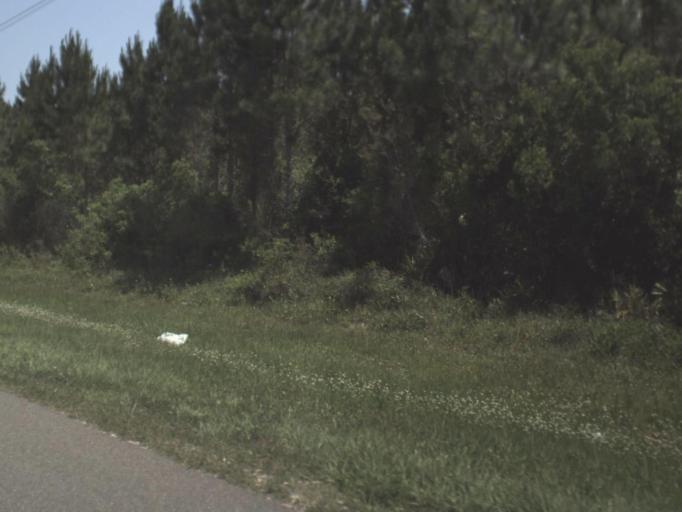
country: US
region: Florida
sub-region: Clay County
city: Keystone Heights
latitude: 29.8282
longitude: -82.0608
